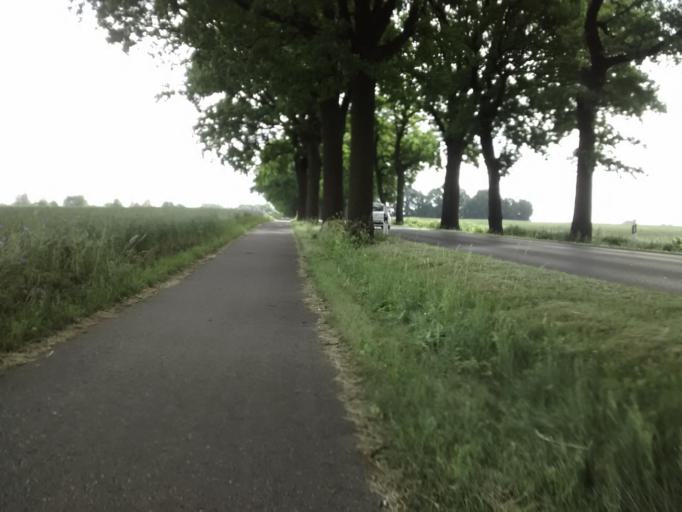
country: DE
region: Brandenburg
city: Glienicke
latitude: 52.6580
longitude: 13.3533
